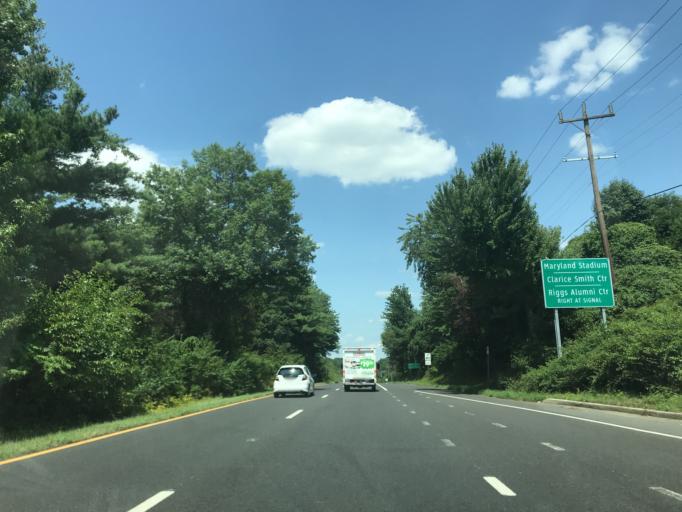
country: US
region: Maryland
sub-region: Prince George's County
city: College Park
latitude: 38.9889
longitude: -76.9540
